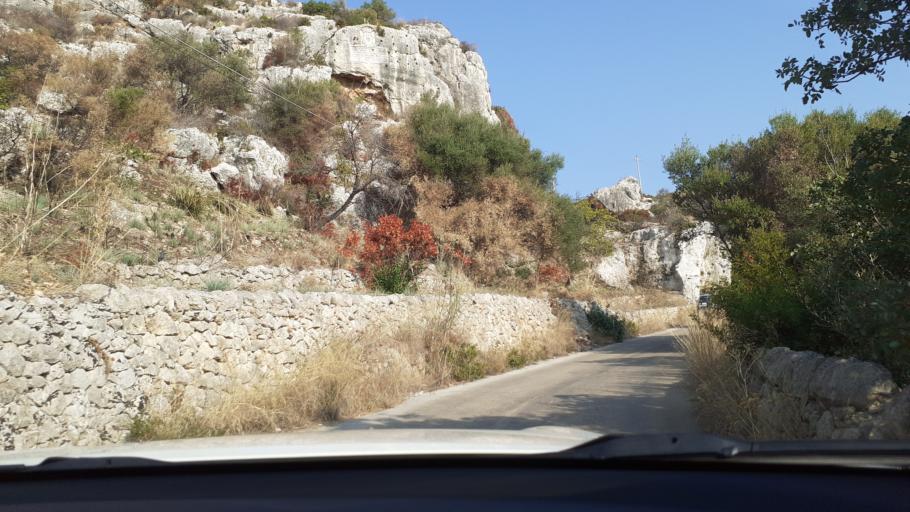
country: IT
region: Sicily
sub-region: Provincia di Siracusa
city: Cassibile
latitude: 36.9794
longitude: 15.1716
